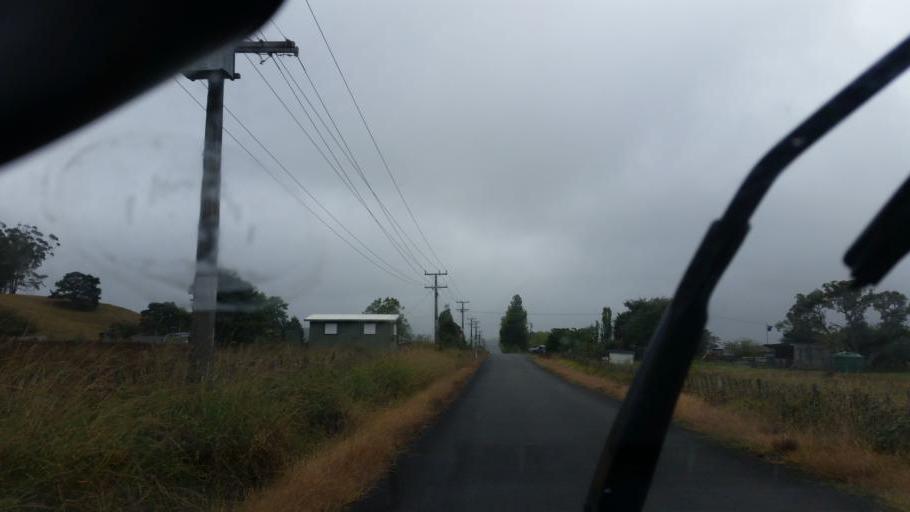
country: NZ
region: Northland
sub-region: Kaipara District
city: Dargaville
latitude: -35.8341
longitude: 173.7524
